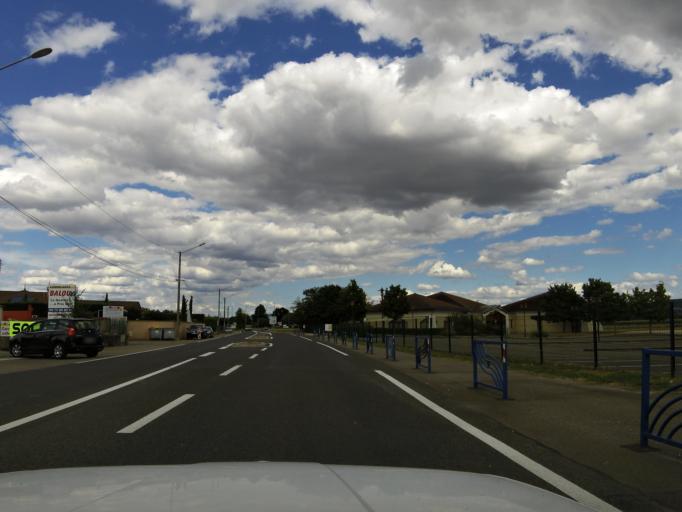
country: FR
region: Rhone-Alpes
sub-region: Departement de l'Ain
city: Loyettes
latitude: 45.7785
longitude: 5.2127
